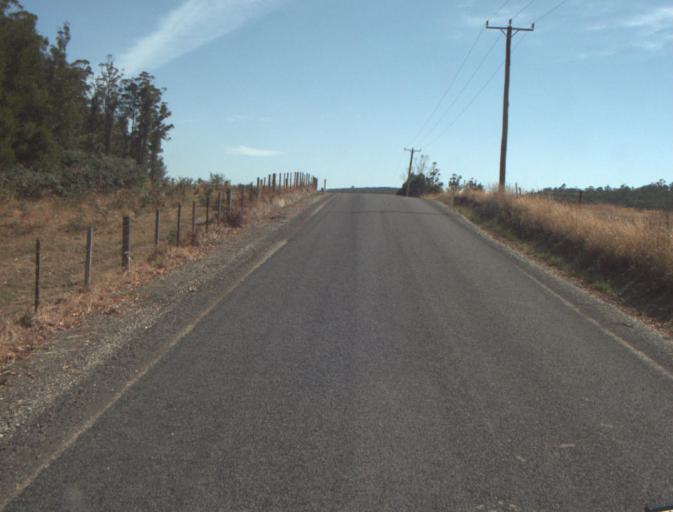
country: AU
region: Tasmania
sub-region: Launceston
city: Mayfield
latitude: -41.2336
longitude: 147.2348
